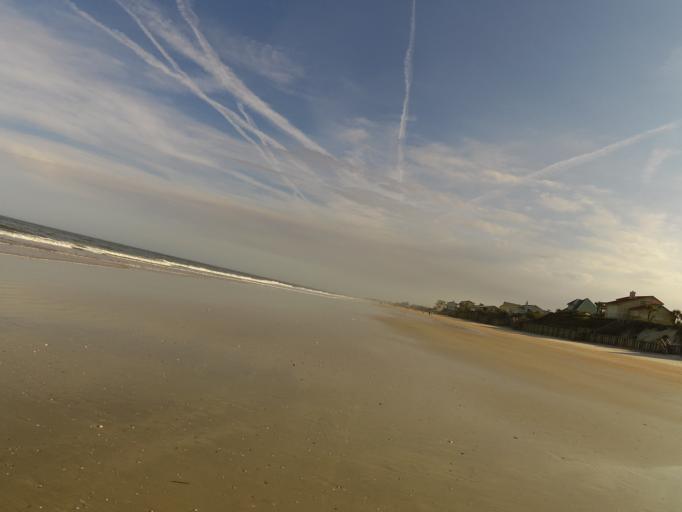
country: US
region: Florida
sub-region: Saint Johns County
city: Villano Beach
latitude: 29.9460
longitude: -81.2989
